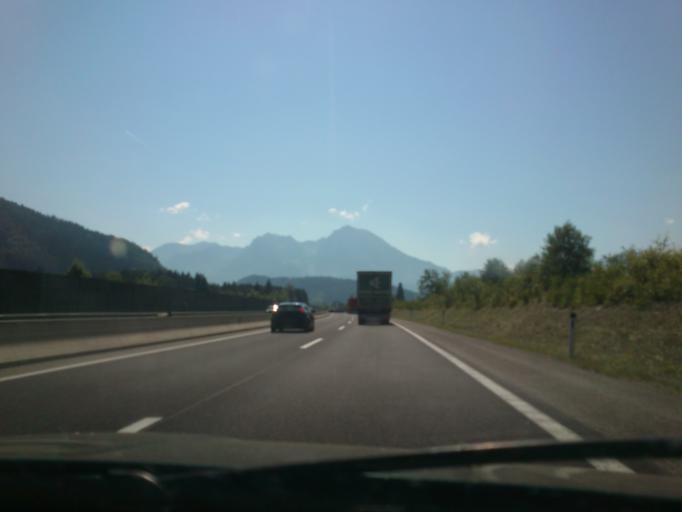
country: AT
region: Upper Austria
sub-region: Politischer Bezirk Kirchdorf an der Krems
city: Rossleithen
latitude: 47.7337
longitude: 14.2924
